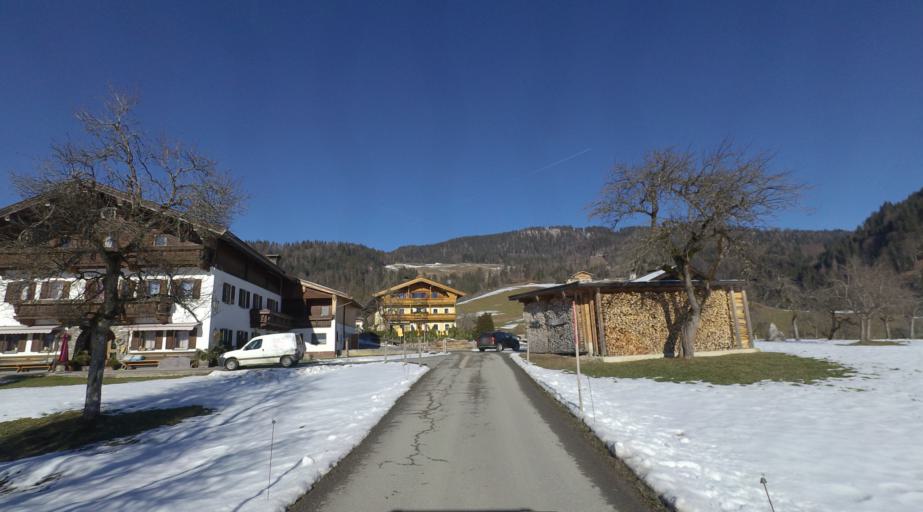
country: AT
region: Tyrol
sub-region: Politischer Bezirk Kitzbuhel
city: Kossen
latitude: 47.6782
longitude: 12.4299
